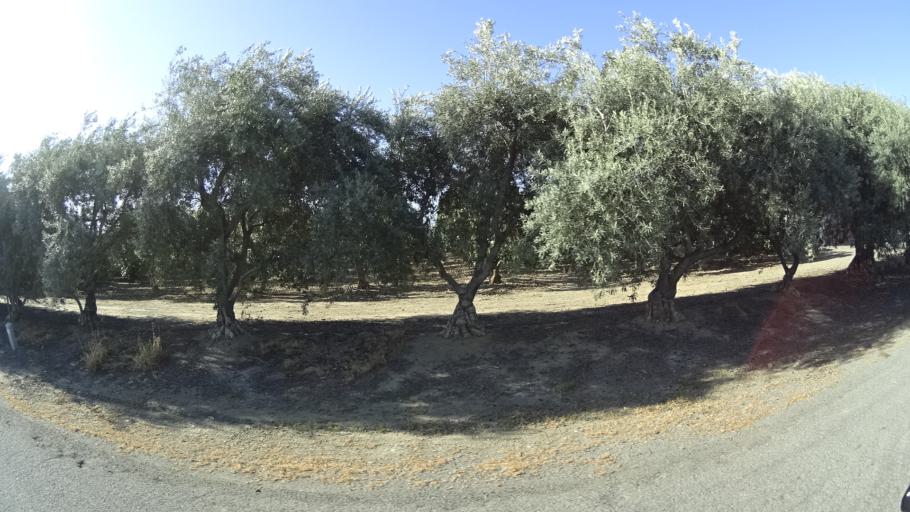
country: US
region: California
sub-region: Glenn County
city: Orland
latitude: 39.7219
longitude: -122.1815
